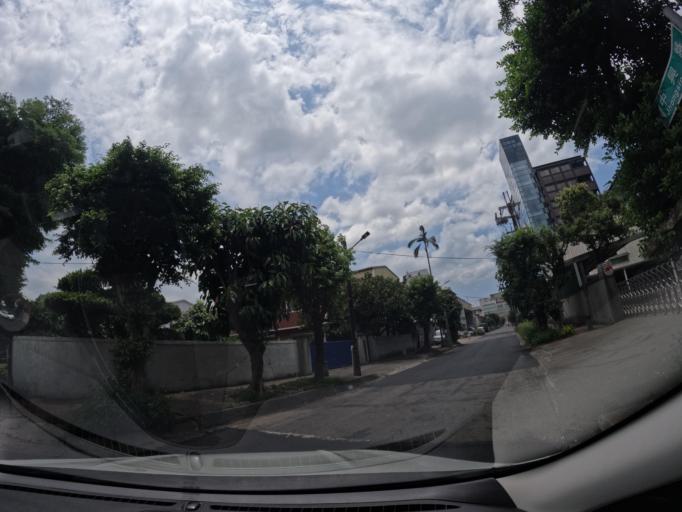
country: TW
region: Taipei
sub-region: Taipei
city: Banqiao
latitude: 24.9671
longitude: 121.4263
